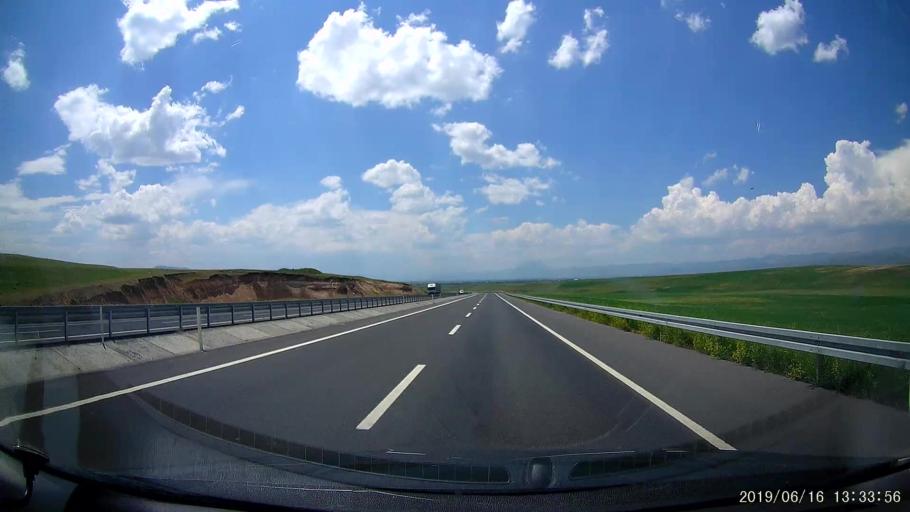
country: TR
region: Agri
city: Agri
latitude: 39.7099
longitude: 43.1407
